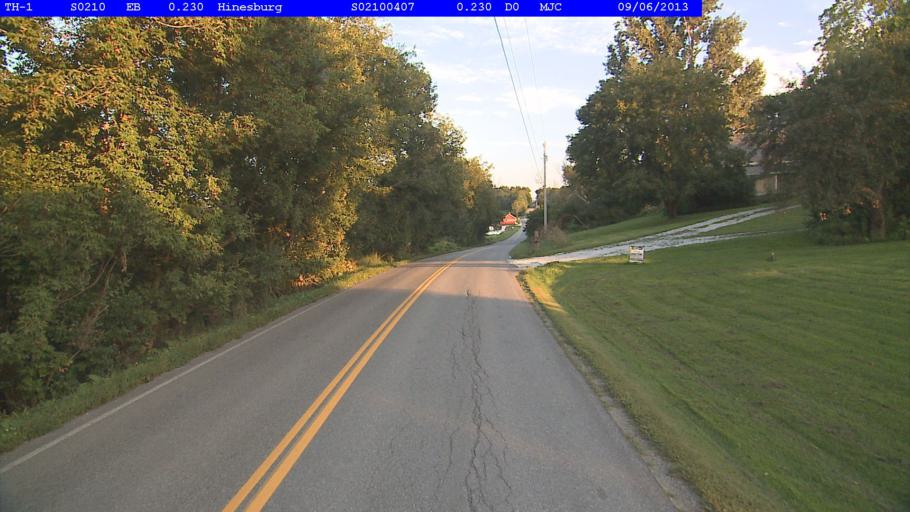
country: US
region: Vermont
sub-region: Chittenden County
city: Hinesburg
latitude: 44.3600
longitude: -73.1587
